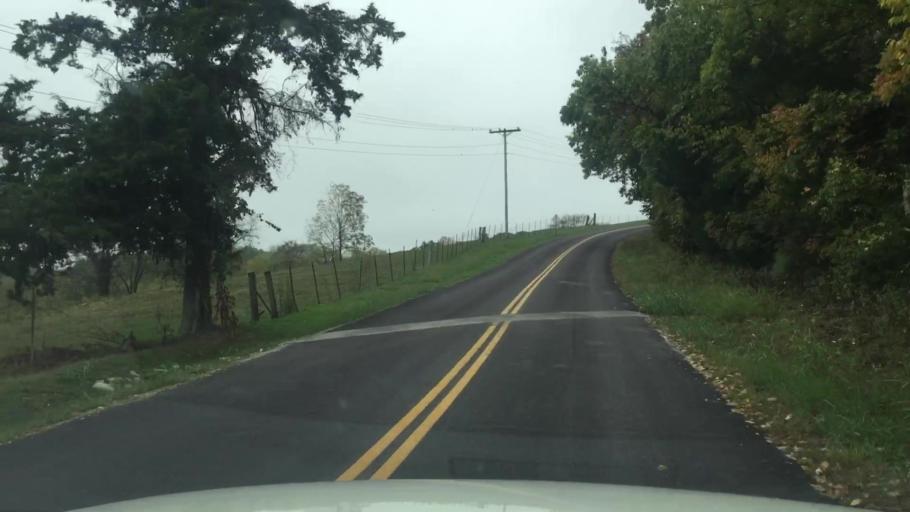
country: US
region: Missouri
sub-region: Boone County
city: Ashland
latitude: 38.8206
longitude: -92.3473
